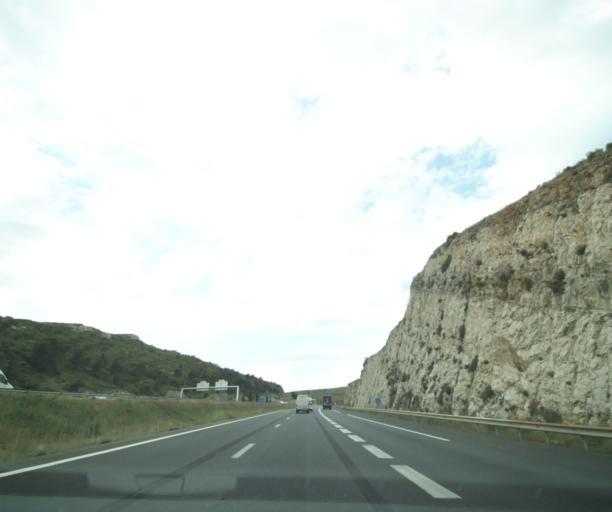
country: FR
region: Provence-Alpes-Cote d'Azur
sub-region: Departement des Bouches-du-Rhone
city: Coudoux
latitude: 43.5600
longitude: 5.2293
